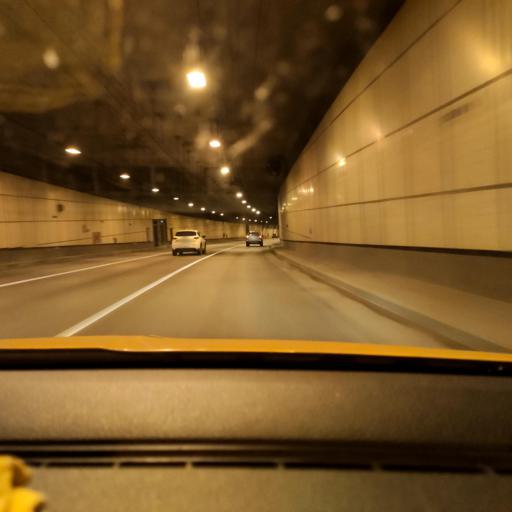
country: RU
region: Moscow
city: Strogino
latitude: 55.7727
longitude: 37.4076
